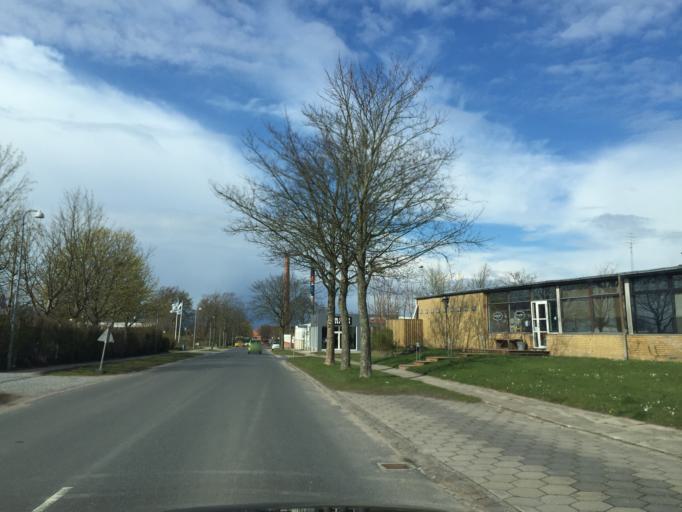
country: DK
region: South Denmark
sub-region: Odense Kommune
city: Odense
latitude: 55.3777
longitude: 10.4140
